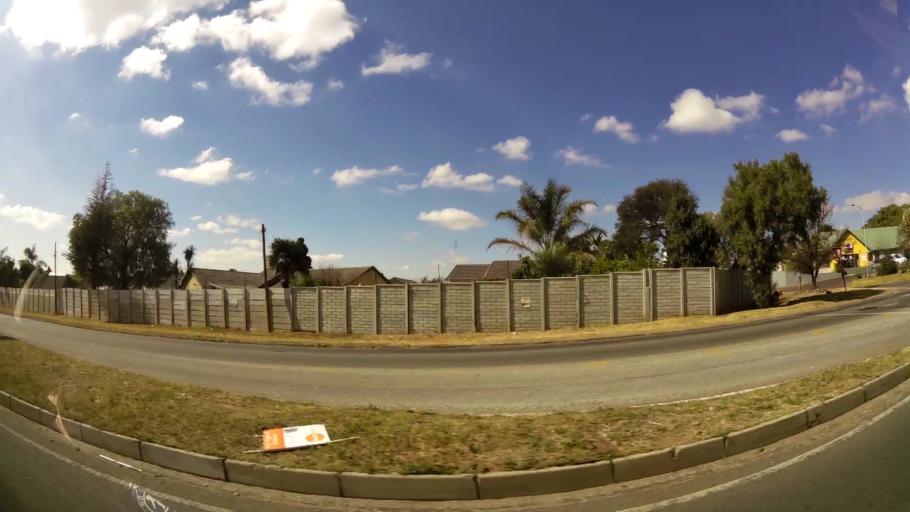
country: ZA
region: Gauteng
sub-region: City of Johannesburg Metropolitan Municipality
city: Roodepoort
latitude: -26.1159
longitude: 27.8514
